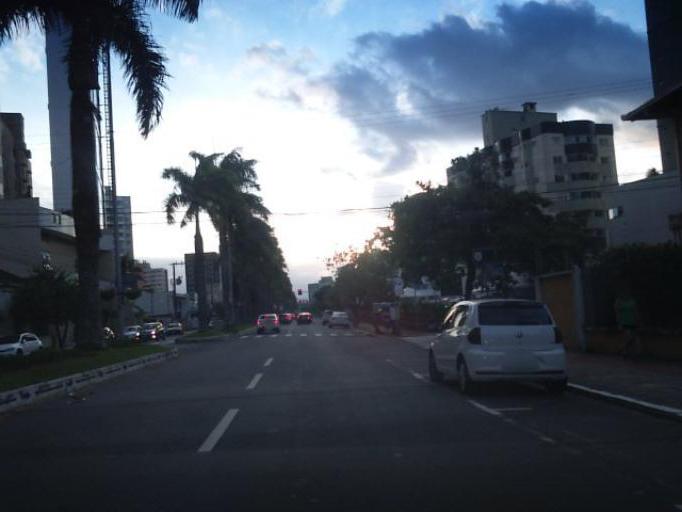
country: BR
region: Santa Catarina
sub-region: Itajai
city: Itajai
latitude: -26.9108
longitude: -48.6552
